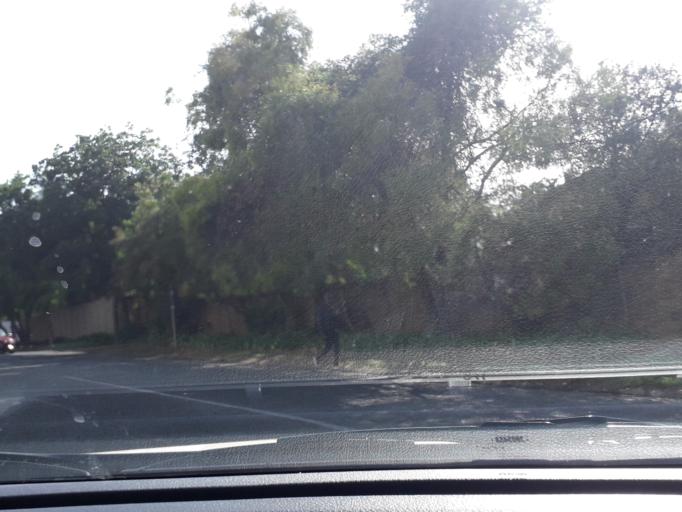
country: ZA
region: Gauteng
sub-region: City of Johannesburg Metropolitan Municipality
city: Johannesburg
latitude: -26.0956
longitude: 28.0371
